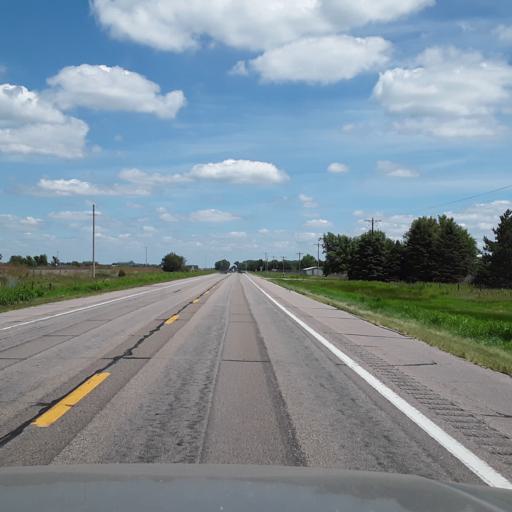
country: US
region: Nebraska
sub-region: Nance County
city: Genoa
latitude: 41.3413
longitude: -97.6037
